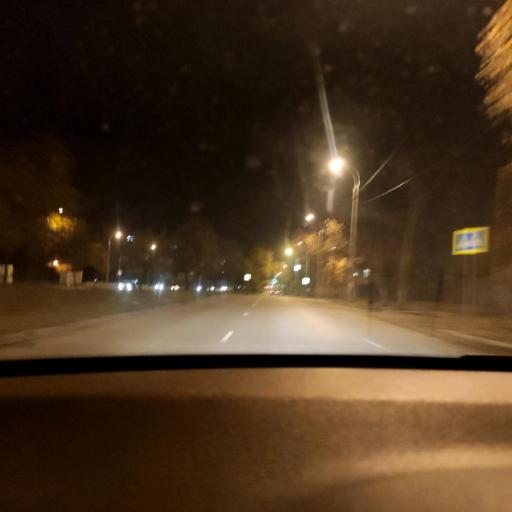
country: RU
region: Samara
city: Samara
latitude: 53.2219
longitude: 50.2367
